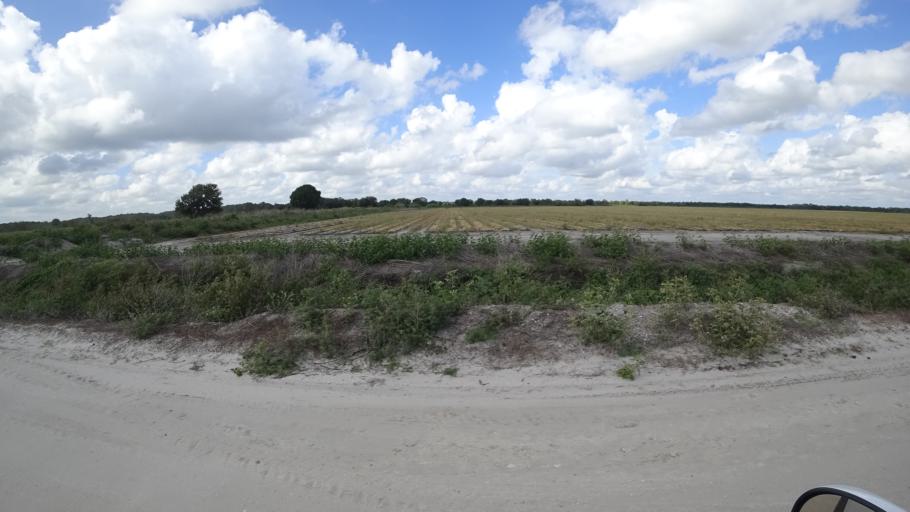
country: US
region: Florida
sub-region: Sarasota County
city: Lake Sarasota
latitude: 27.4299
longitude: -82.1825
